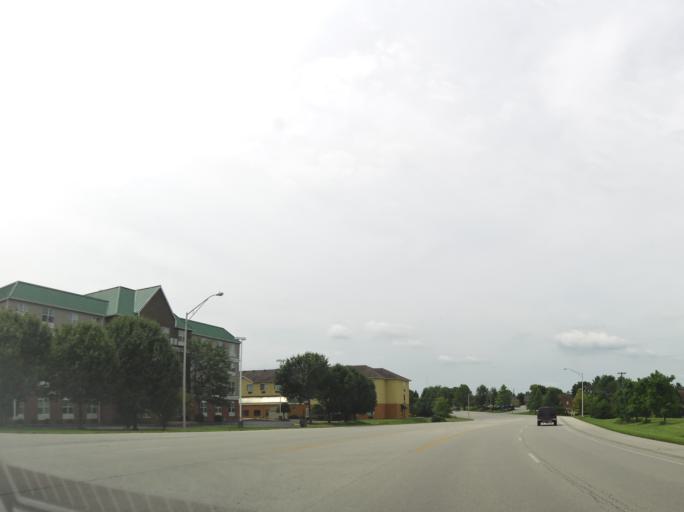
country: US
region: Kentucky
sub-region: Scott County
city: Georgetown
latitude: 38.2245
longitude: -84.5419
